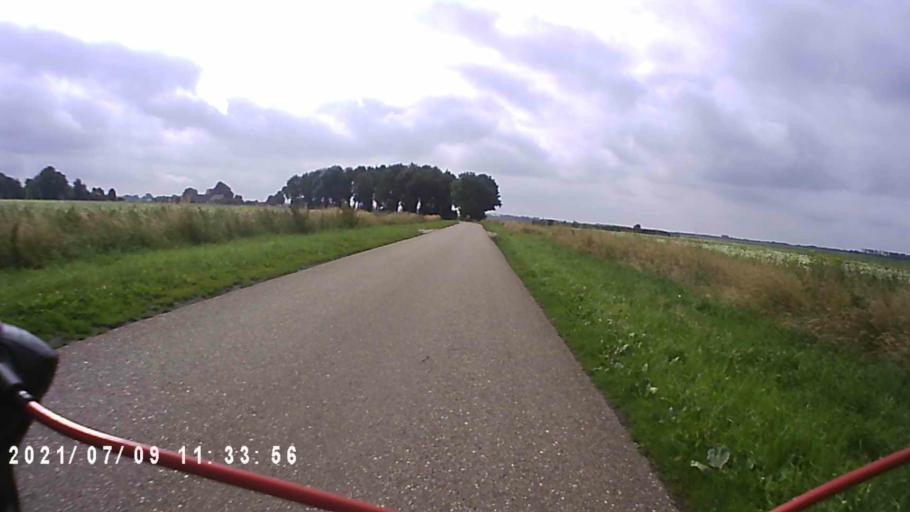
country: NL
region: Groningen
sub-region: Gemeente Slochteren
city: Slochteren
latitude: 53.2273
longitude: 6.8552
